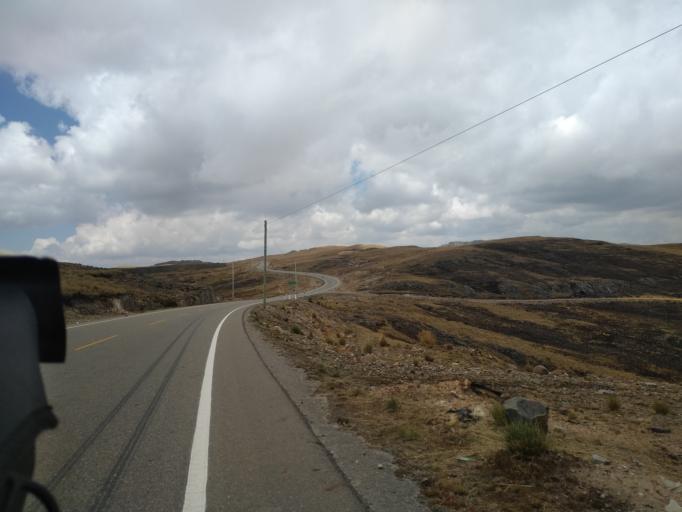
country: PE
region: La Libertad
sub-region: Provincia de Santiago de Chuco
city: Quiruvilca
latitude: -7.9603
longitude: -78.1961
